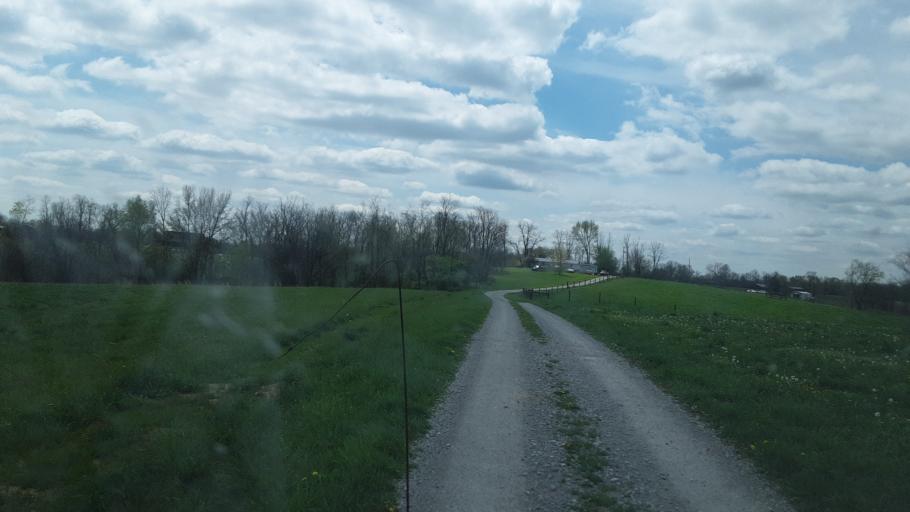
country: US
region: Kentucky
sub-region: Gallatin County
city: Warsaw
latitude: 38.6773
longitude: -84.8121
